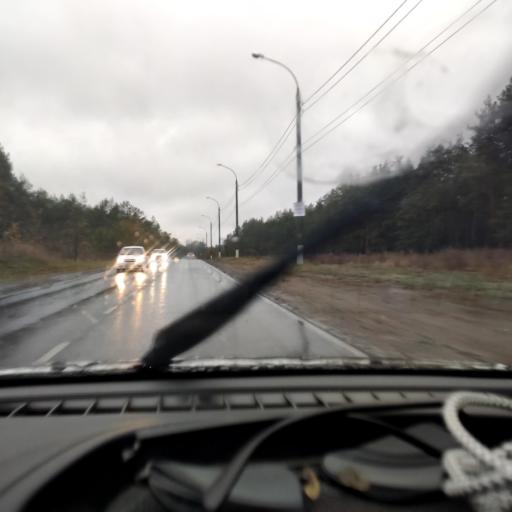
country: RU
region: Samara
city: Zhigulevsk
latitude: 53.4776
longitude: 49.4462
